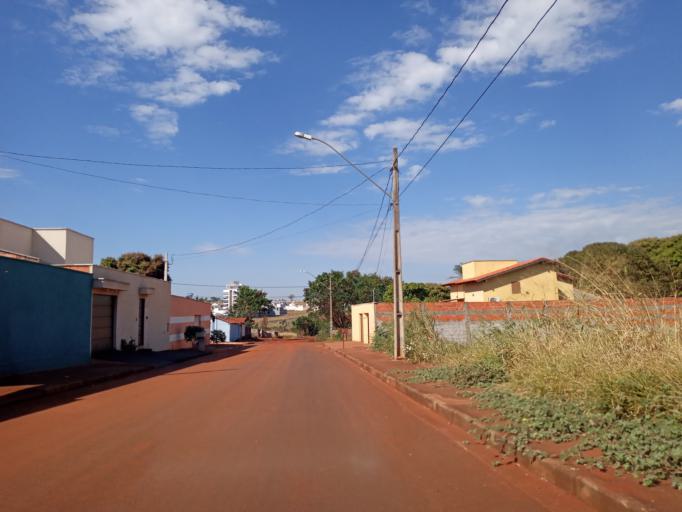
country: BR
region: Minas Gerais
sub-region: Ituiutaba
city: Ituiutaba
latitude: -18.9961
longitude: -49.4644
